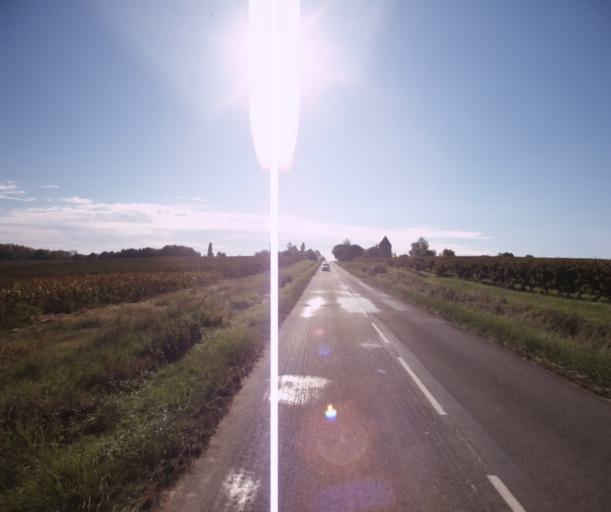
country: FR
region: Aquitaine
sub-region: Departement des Landes
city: Gabarret
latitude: 43.9183
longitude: 0.0184
